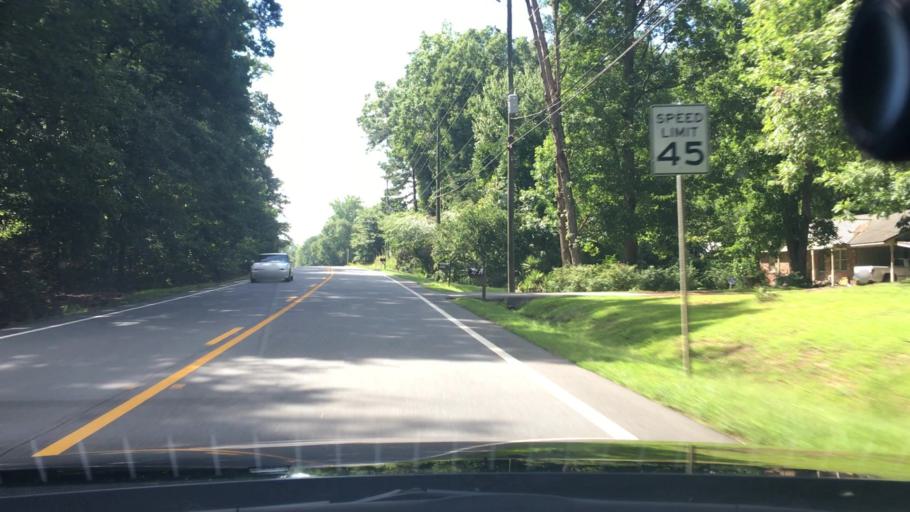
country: US
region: Georgia
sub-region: Butts County
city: Jackson
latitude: 33.2914
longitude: -83.9425
